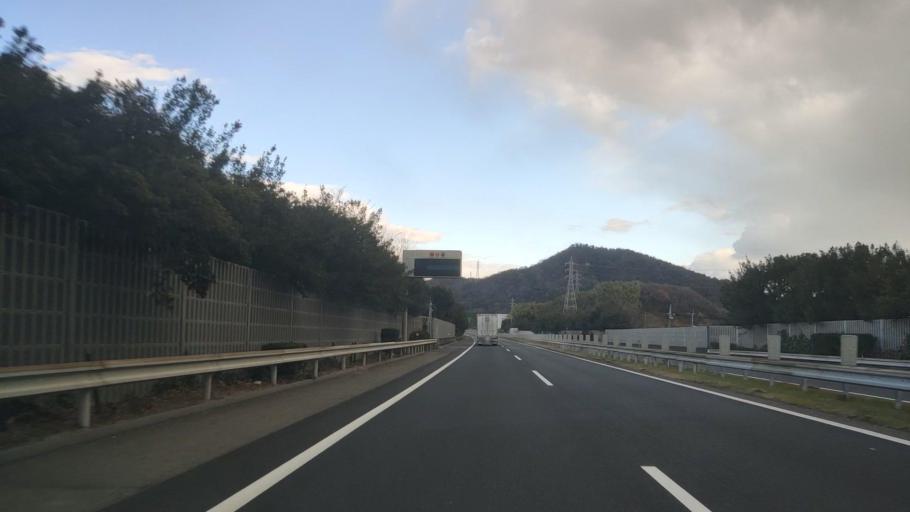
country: JP
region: Okayama
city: Kamogatacho-kamogata
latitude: 34.5519
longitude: 133.5836
